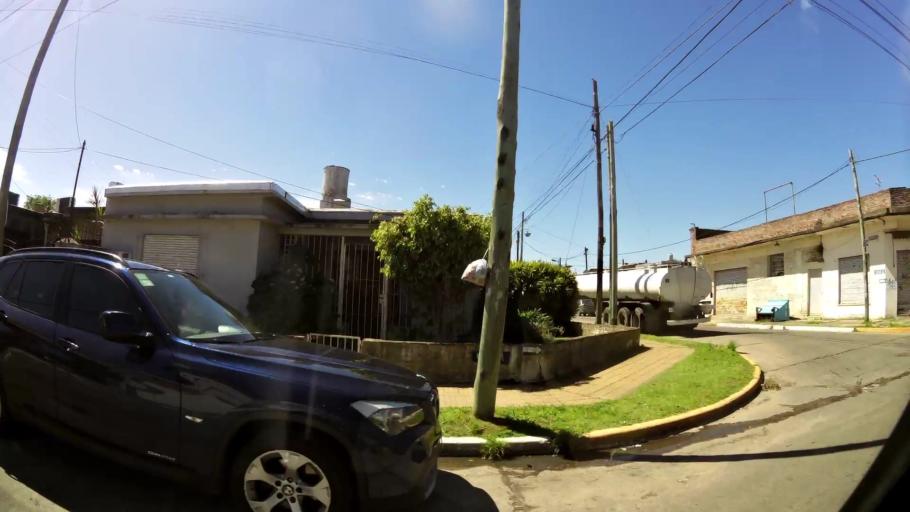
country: AR
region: Buenos Aires
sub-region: Partido de Quilmes
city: Quilmes
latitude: -34.7014
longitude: -58.2849
